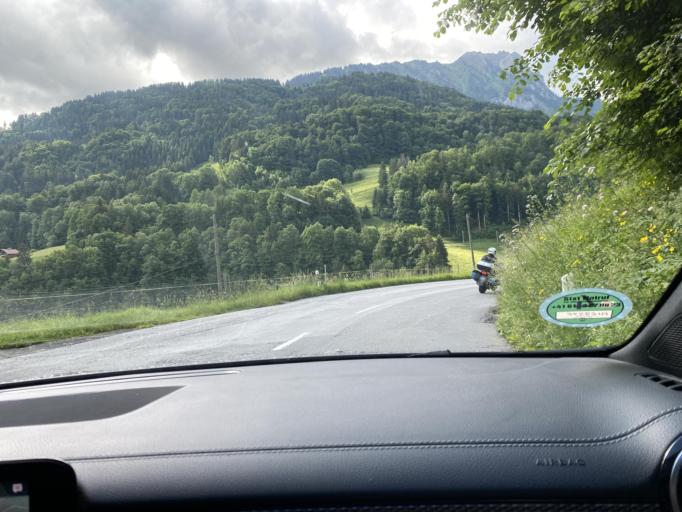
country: CH
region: Vaud
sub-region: Aigle District
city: Leysin
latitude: 46.3547
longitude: 7.0488
